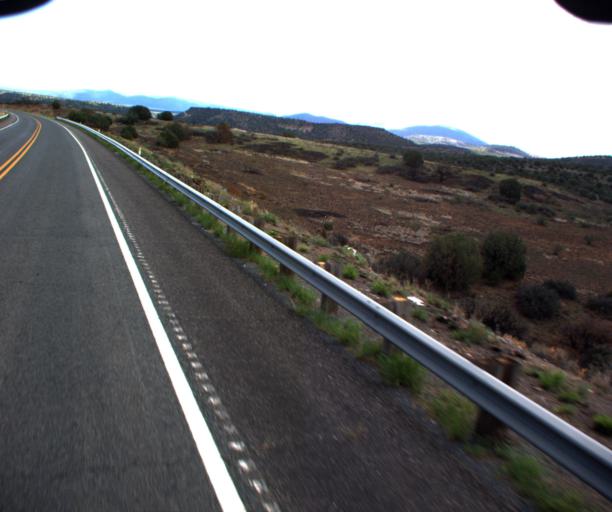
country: US
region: Arizona
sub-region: Yavapai County
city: Camp Verde
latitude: 34.5148
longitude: -112.0185
